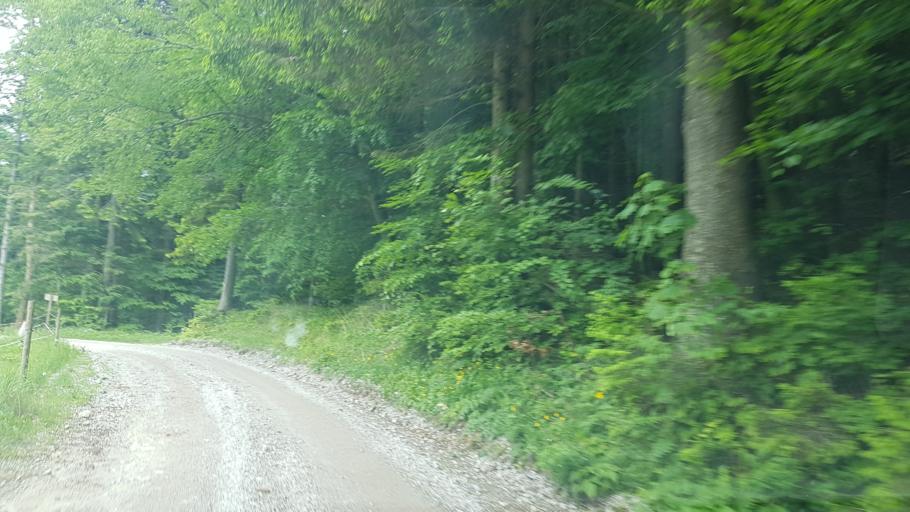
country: SI
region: Dobrna
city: Dobrna
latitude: 46.3813
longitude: 15.2346
